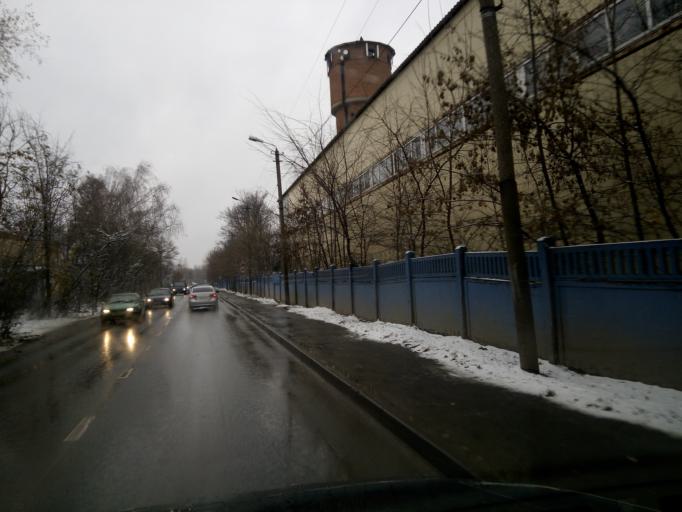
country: RU
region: Moskovskaya
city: Skhodnya
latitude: 55.9435
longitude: 37.2811
